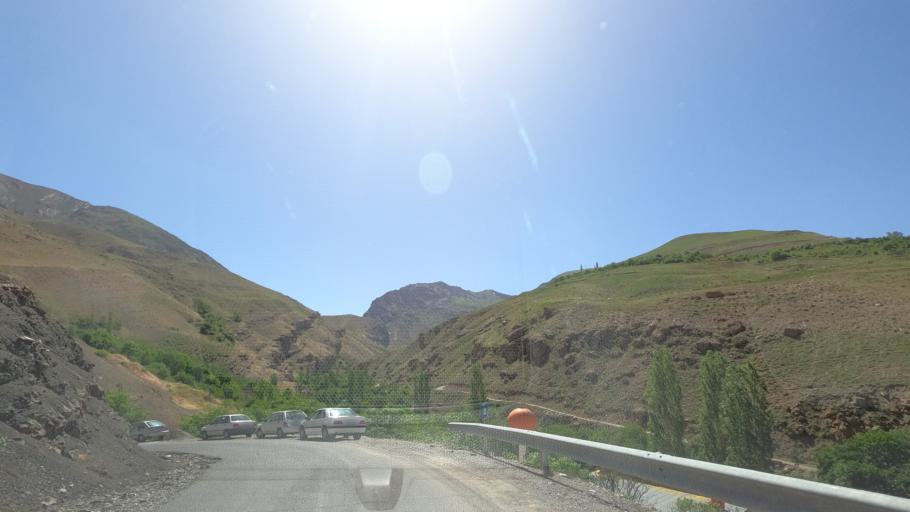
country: IR
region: Alborz
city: Karaj
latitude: 35.9265
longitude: 51.1564
